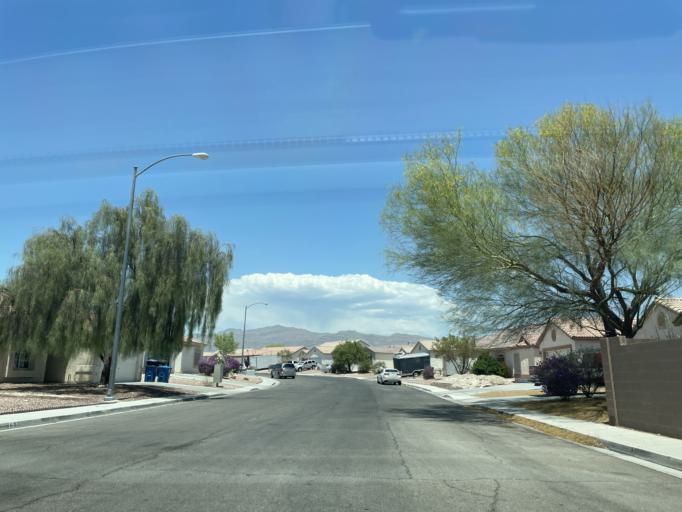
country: US
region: Nevada
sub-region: Clark County
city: North Las Vegas
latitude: 36.2624
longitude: -115.1503
